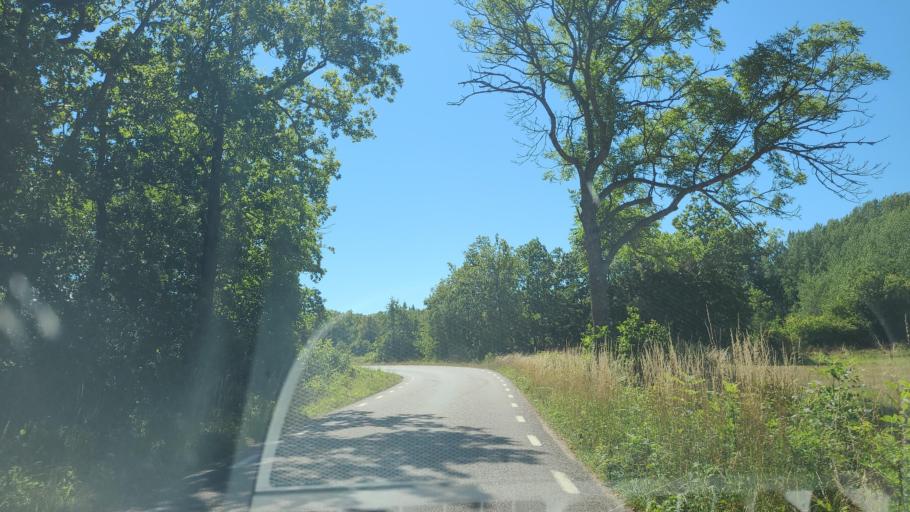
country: SE
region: Kalmar
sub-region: Borgholms Kommun
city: Borgholm
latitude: 56.7473
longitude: 16.6598
